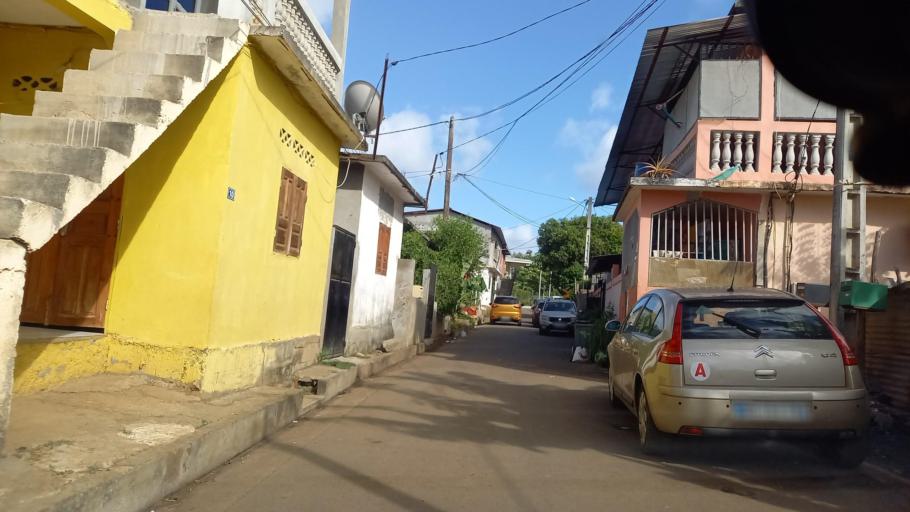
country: YT
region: Bandrele
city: Bandrele
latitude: -12.9107
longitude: 45.1937
